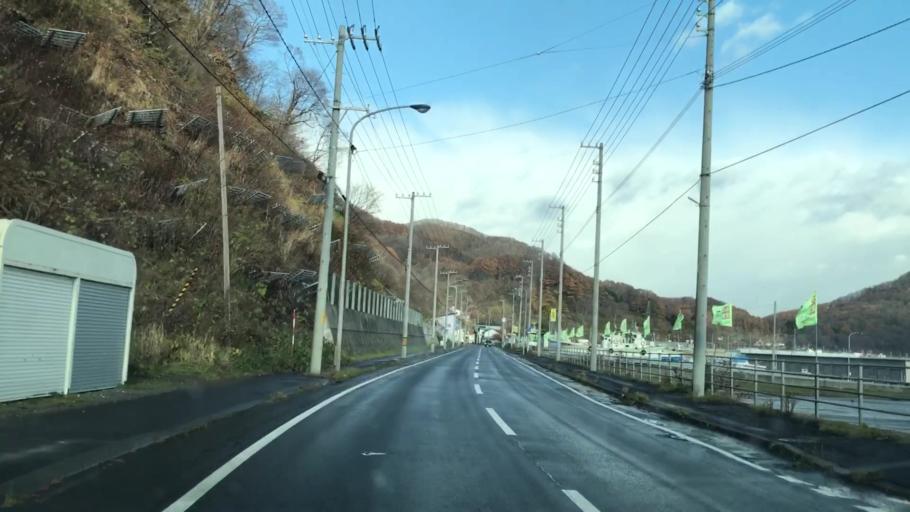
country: JP
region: Hokkaido
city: Yoichi
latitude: 43.2690
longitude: 140.6379
